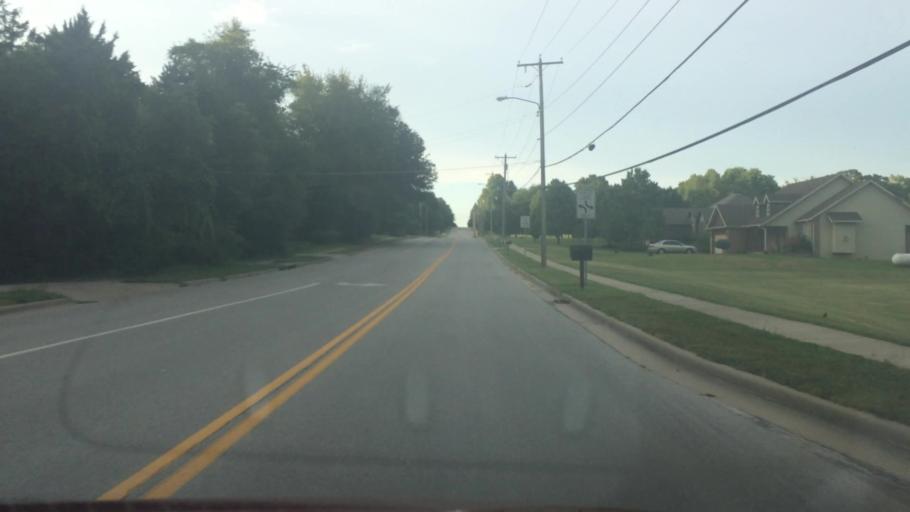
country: US
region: Missouri
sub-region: Greene County
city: Strafford
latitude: 37.1977
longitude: -93.1890
